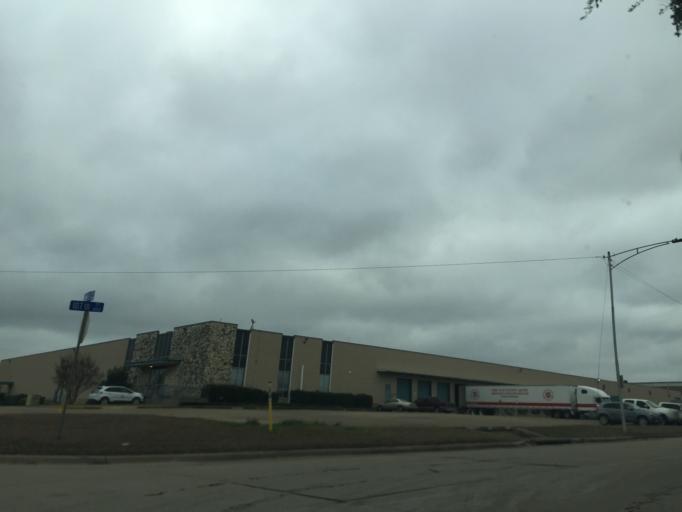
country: US
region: Texas
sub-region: Tarrant County
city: Arlington
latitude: 32.7564
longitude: -97.0574
